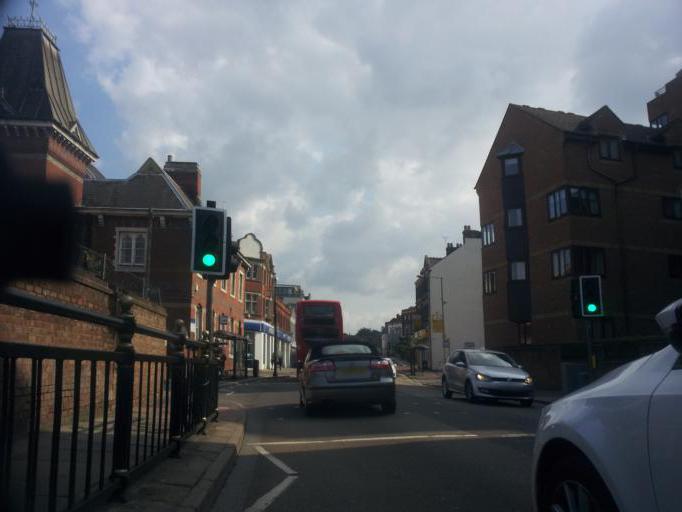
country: GB
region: England
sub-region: Medway
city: Rochester
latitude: 51.3856
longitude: 0.5083
